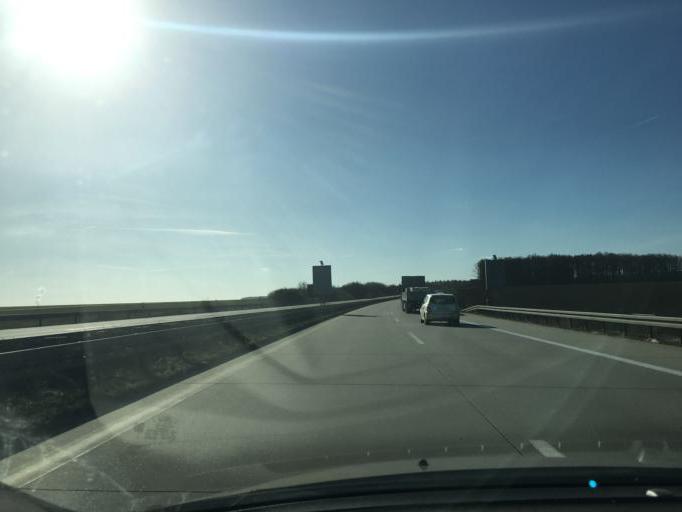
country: DE
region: Saxony
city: Niederfrohna
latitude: 50.9023
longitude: 12.7383
